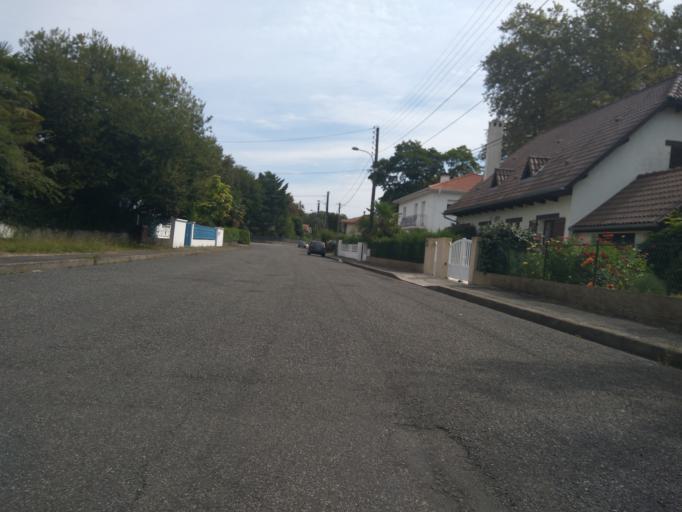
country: FR
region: Aquitaine
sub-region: Departement des Pyrenees-Atlantiques
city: Bizanos
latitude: 43.2939
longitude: -0.3511
